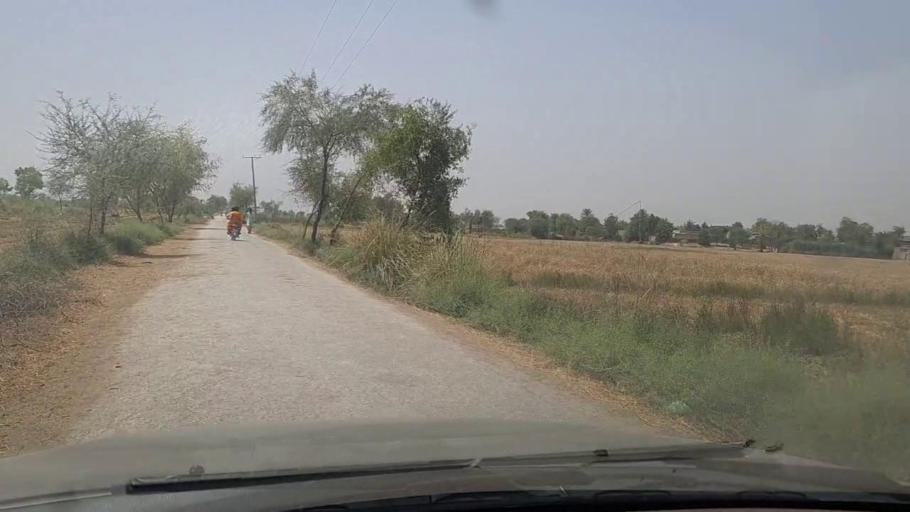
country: PK
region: Sindh
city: Miro Khan
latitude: 27.7631
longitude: 68.1202
